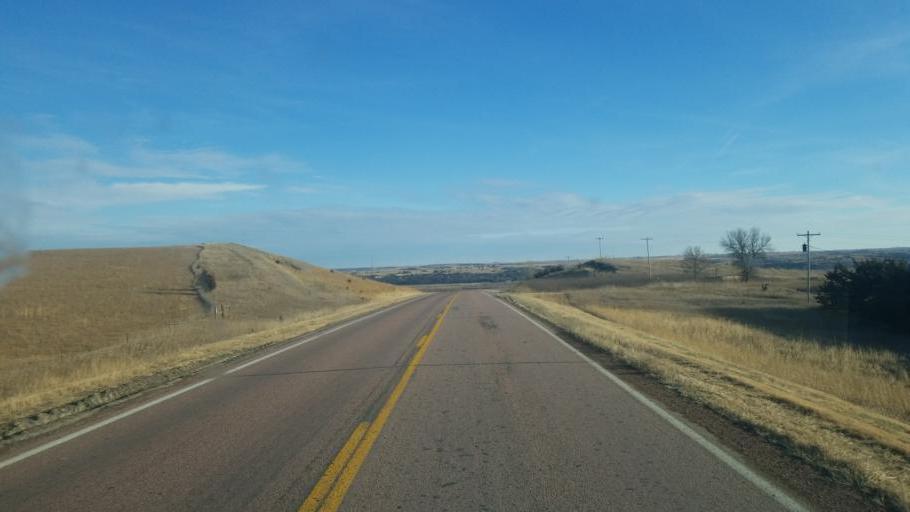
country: US
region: South Dakota
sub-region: Bon Homme County
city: Springfield
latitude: 42.7531
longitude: -98.0721
